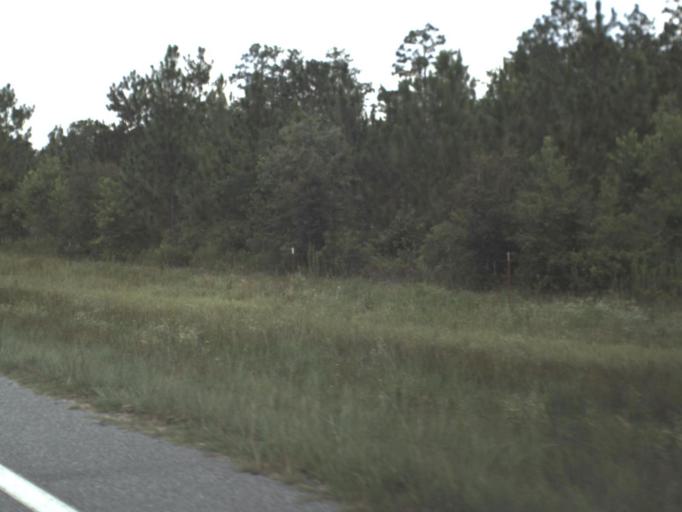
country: US
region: Florida
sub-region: Madison County
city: Madison
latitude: 30.4866
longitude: -83.1944
